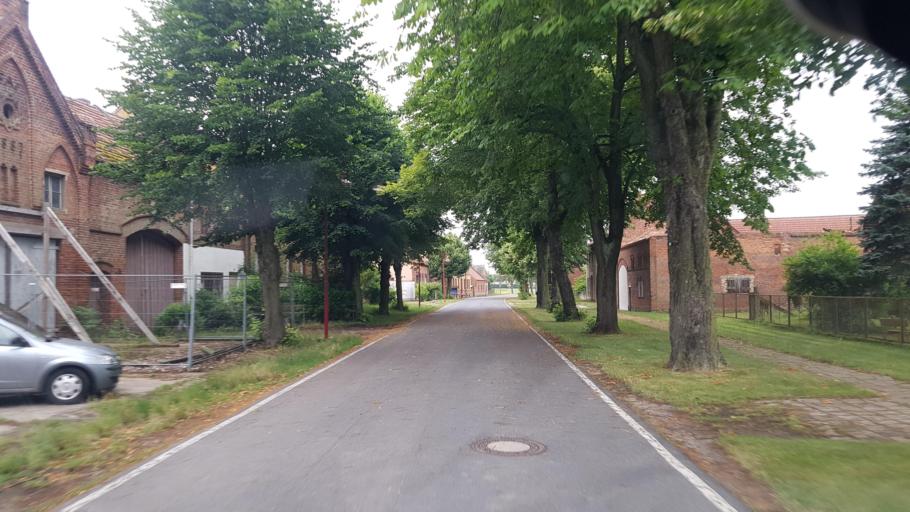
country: DE
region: Brandenburg
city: Ihlow
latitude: 51.9339
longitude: 13.2067
